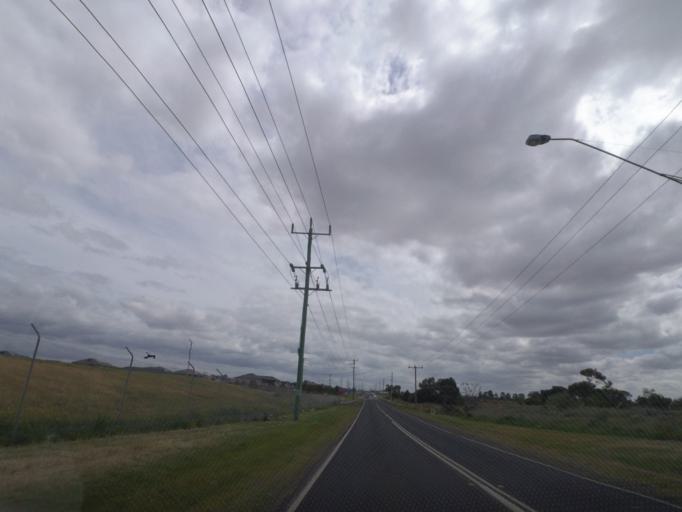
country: AU
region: Victoria
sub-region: Wyndham
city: Williams Landing
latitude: -37.8547
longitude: 144.7542
